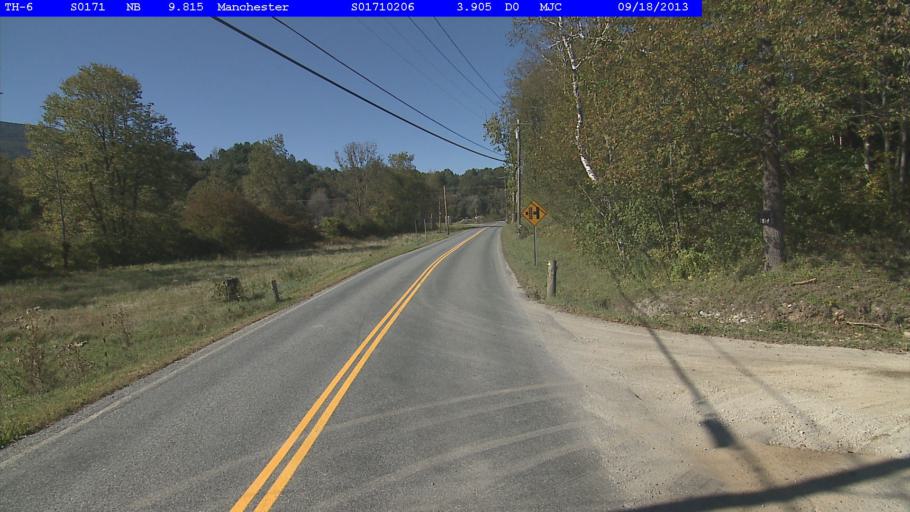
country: US
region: Vermont
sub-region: Bennington County
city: Manchester Center
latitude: 43.1604
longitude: -73.0535
